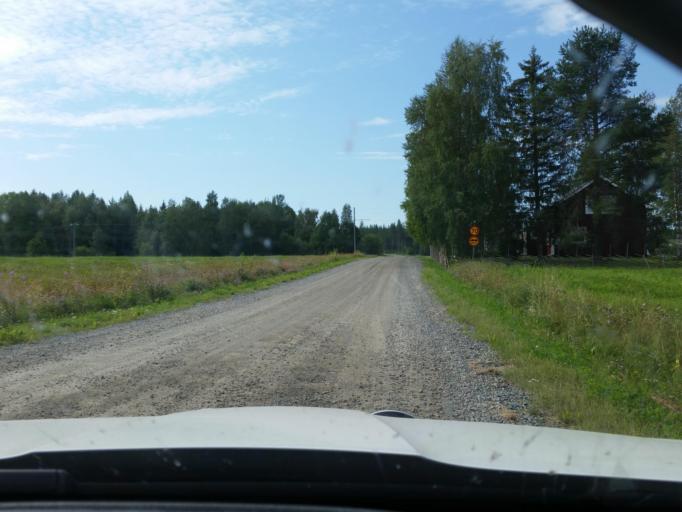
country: SE
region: Norrbotten
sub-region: Alvsbyns Kommun
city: AElvsbyn
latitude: 65.7467
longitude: 20.8895
